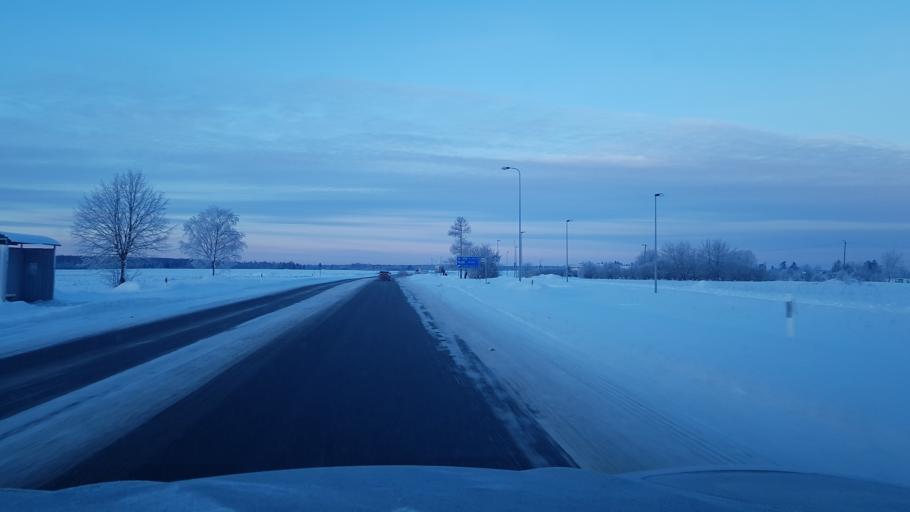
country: EE
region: Ida-Virumaa
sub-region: Narva linn
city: Narva
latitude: 59.3893
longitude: 28.1336
